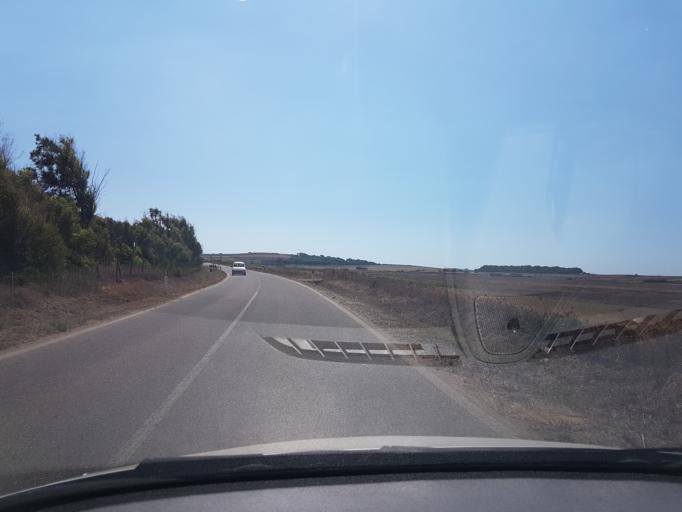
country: IT
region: Sardinia
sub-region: Provincia di Oristano
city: Nurachi
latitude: 39.9903
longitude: 8.4611
